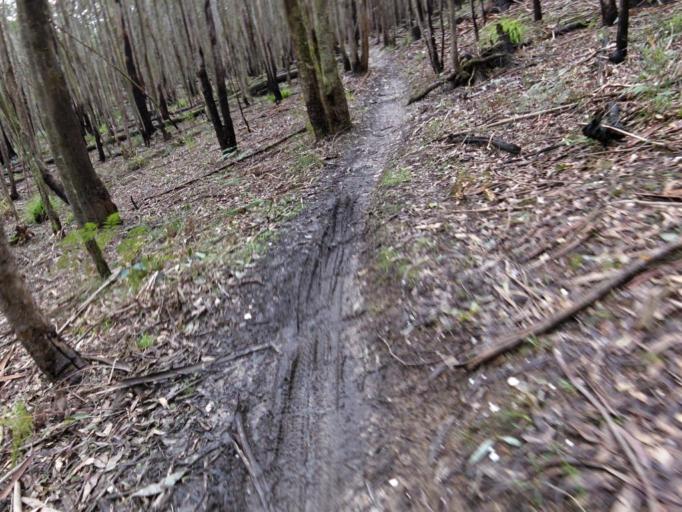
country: AU
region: Victoria
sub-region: Moorabool
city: Bacchus Marsh
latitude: -37.4158
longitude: 144.4947
